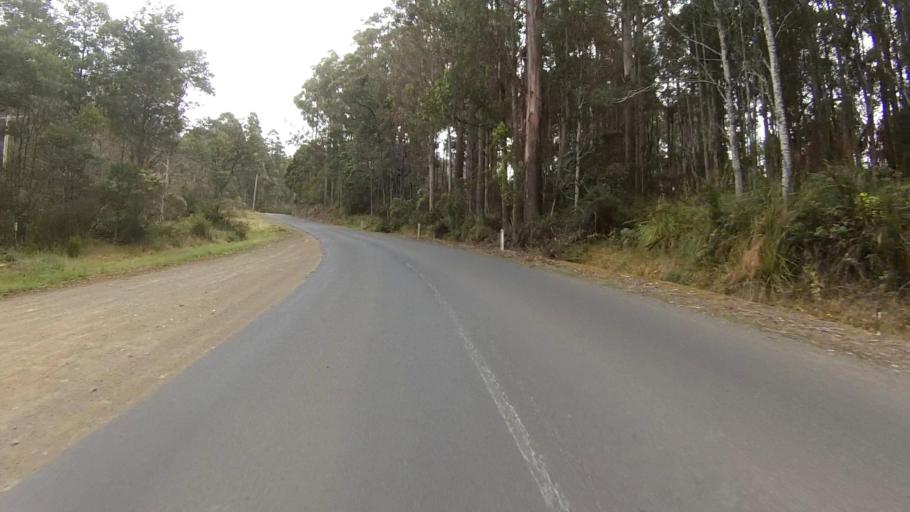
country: AU
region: Tasmania
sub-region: Huon Valley
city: Cygnet
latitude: -43.1409
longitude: 147.1534
